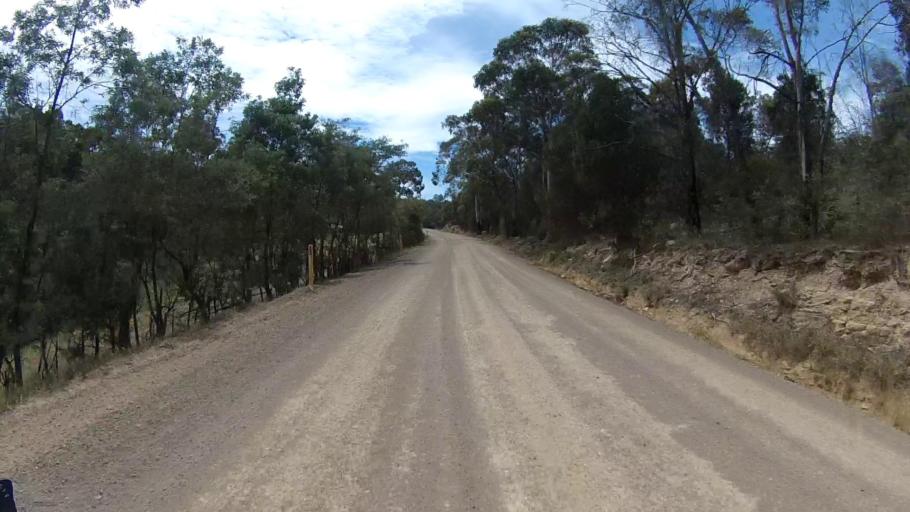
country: AU
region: Tasmania
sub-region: Sorell
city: Sorell
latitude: -42.8009
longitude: 147.6591
